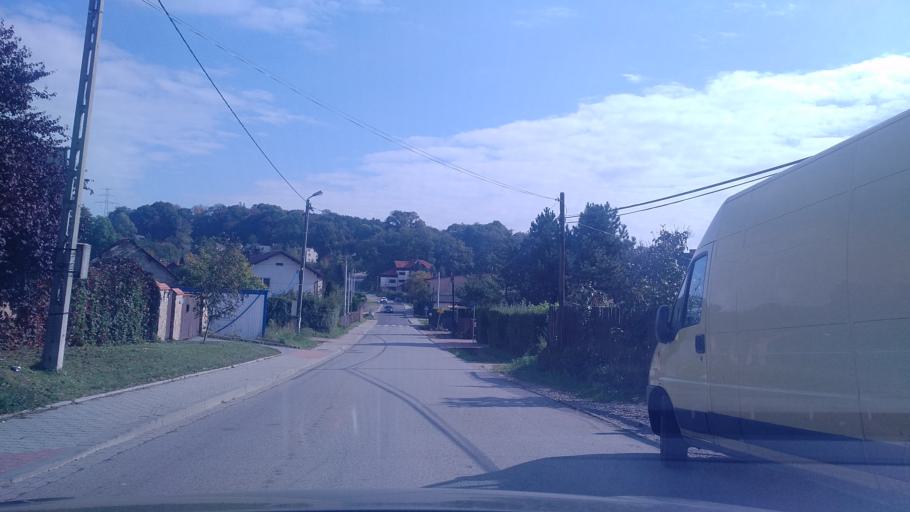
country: PL
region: Lesser Poland Voivodeship
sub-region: Powiat krakowski
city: Modlnica
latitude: 50.1331
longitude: 19.8573
